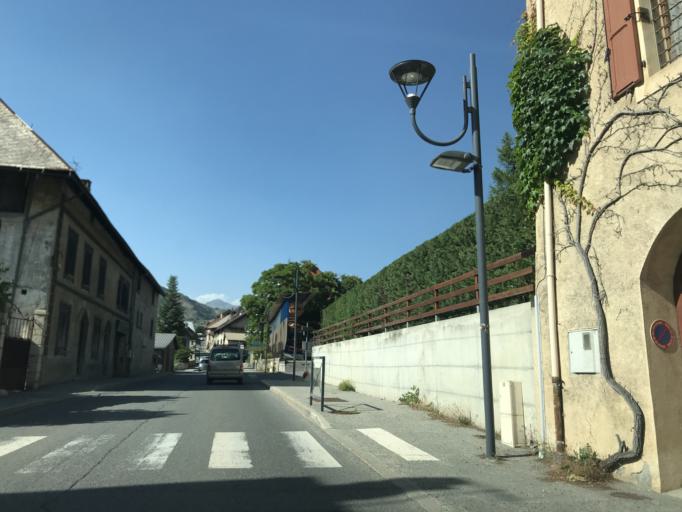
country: FR
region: Provence-Alpes-Cote d'Azur
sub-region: Departement des Hautes-Alpes
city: Saint-Martin-de-Queyrieres
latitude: 44.7930
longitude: 6.5623
